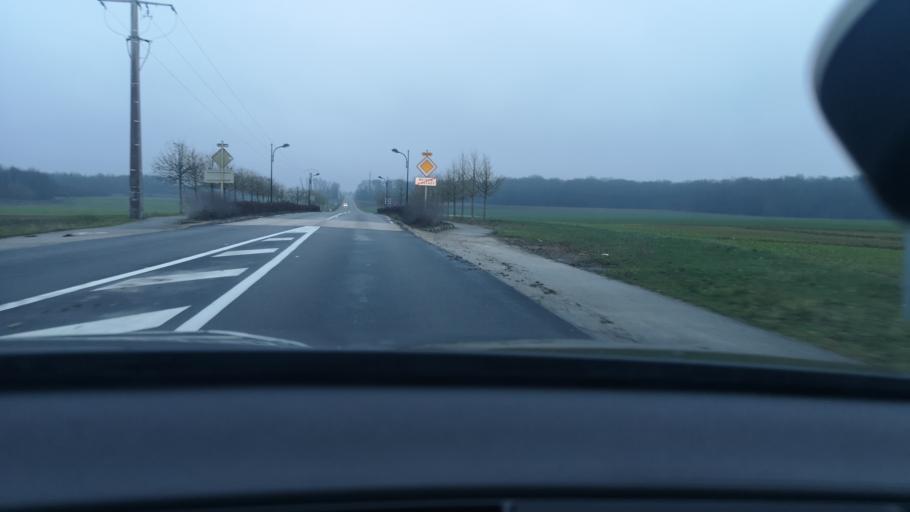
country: FR
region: Bourgogne
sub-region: Departement de la Cote-d'Or
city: Fenay
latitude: 47.1885
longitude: 5.0789
